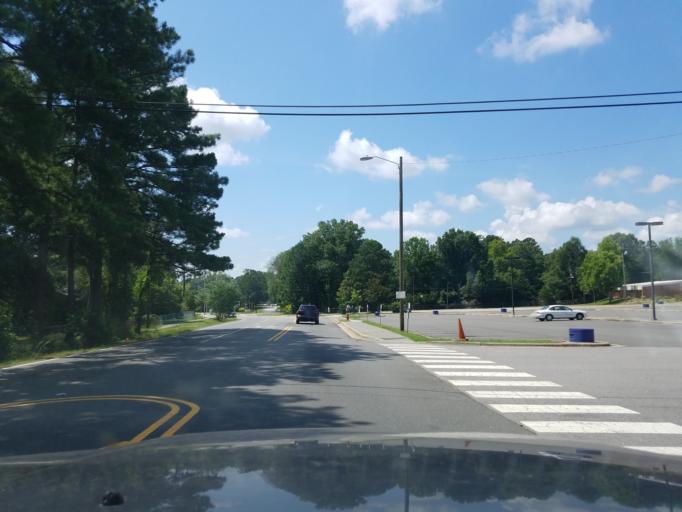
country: US
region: North Carolina
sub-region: Durham County
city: Durham
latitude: 35.9228
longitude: -78.9610
